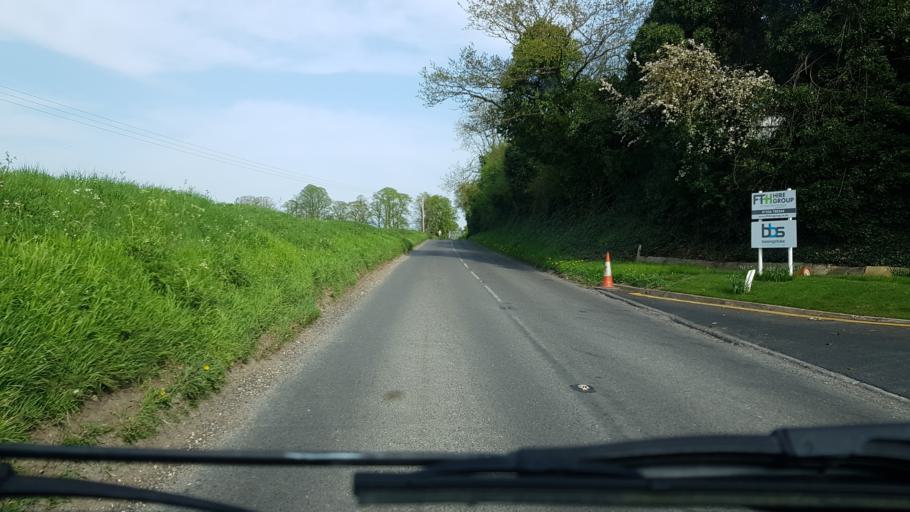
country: GB
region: England
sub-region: Hampshire
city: Overton
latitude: 51.2556
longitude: -1.1880
